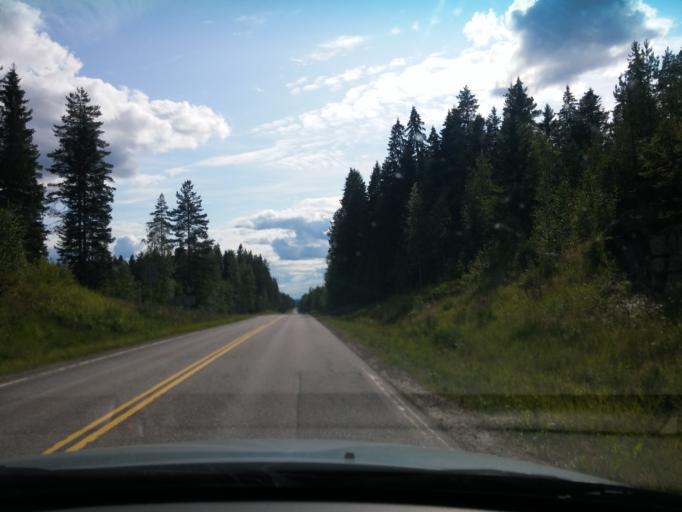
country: FI
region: Central Finland
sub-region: Keuruu
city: Keuruu
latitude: 62.3054
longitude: 24.7254
